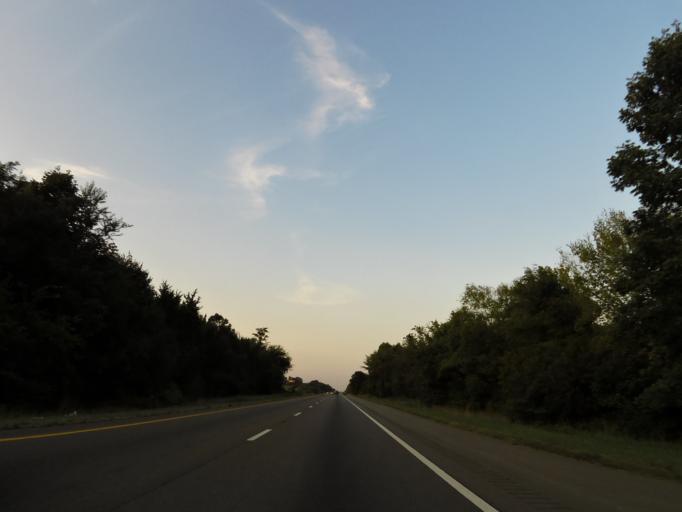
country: US
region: Tennessee
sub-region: Loudon County
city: Lenoir City
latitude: 35.8031
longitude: -84.3120
